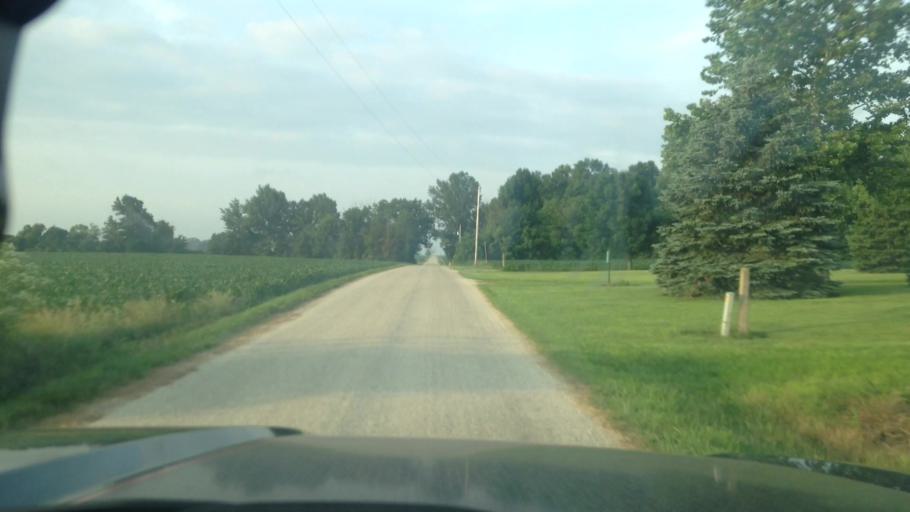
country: US
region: Indiana
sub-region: Randolph County
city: Union City
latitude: 40.2427
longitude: -84.8625
